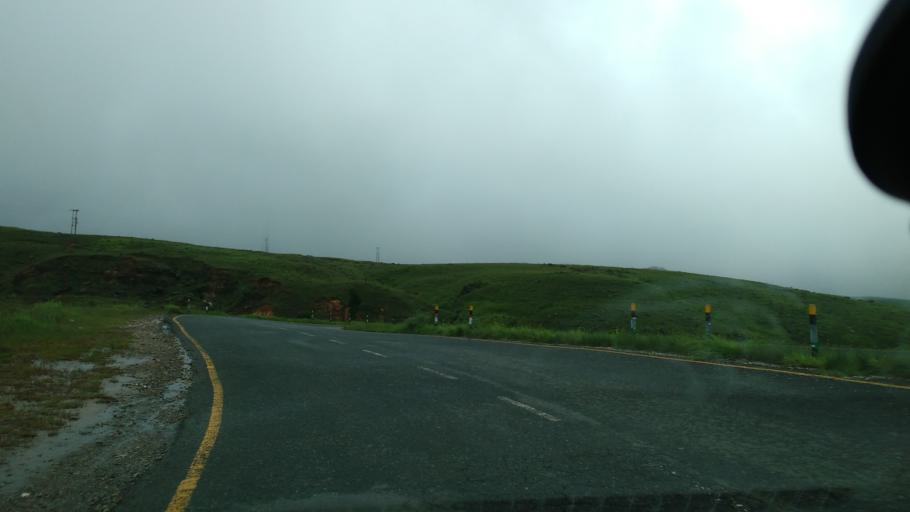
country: IN
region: Meghalaya
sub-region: East Khasi Hills
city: Cherrapunji
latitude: 25.3215
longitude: 91.7341
